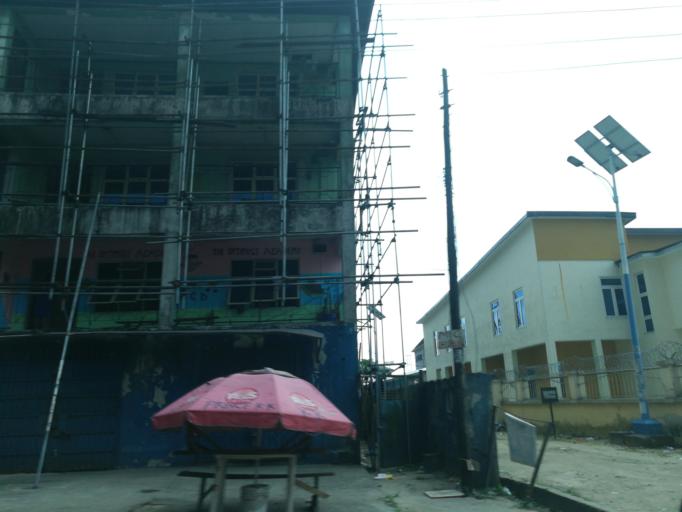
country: NG
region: Rivers
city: Port Harcourt
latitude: 4.8039
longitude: 6.9891
